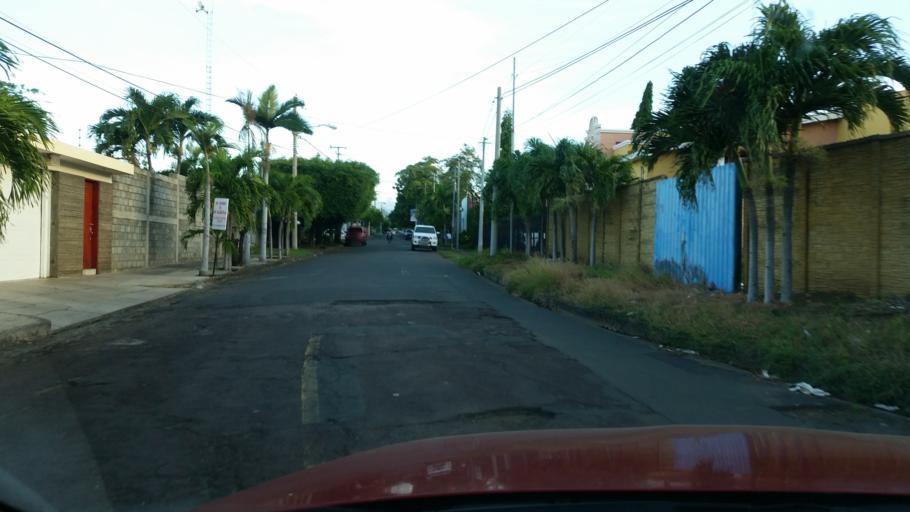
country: NI
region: Managua
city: Managua
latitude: 12.1418
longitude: -86.2851
